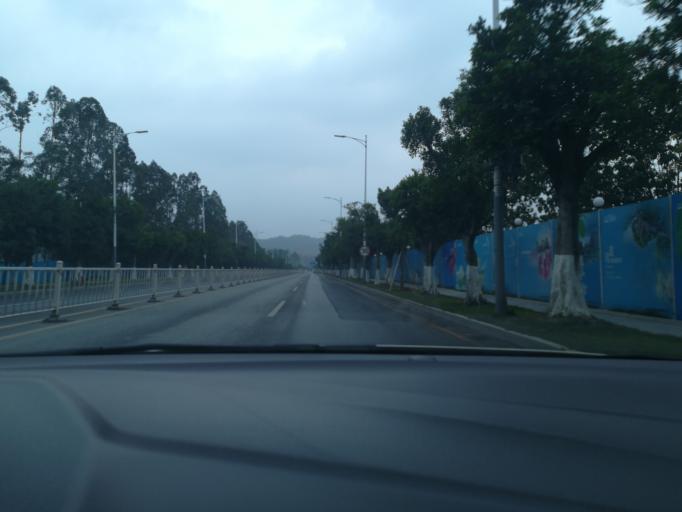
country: CN
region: Guangdong
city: Nansha
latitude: 22.7758
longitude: 113.5955
